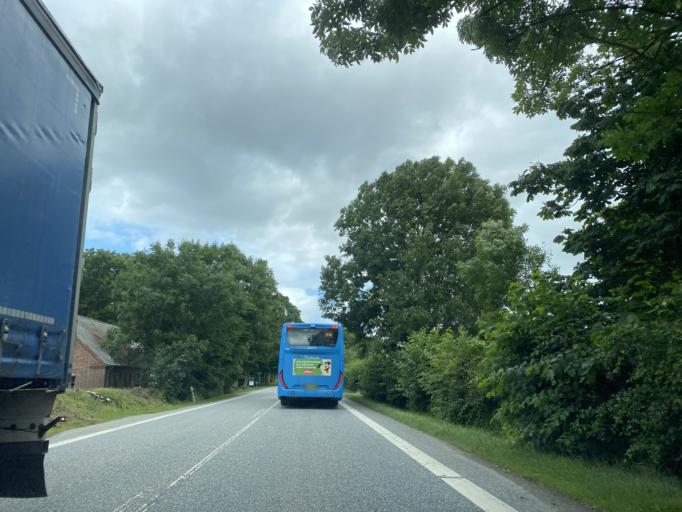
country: DK
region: Central Jutland
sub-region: Silkeborg Kommune
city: Silkeborg
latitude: 56.2528
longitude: 9.6271
